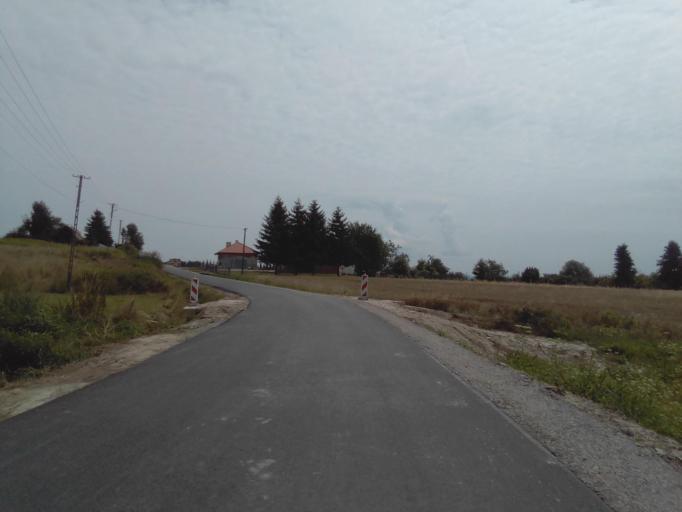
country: PL
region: Subcarpathian Voivodeship
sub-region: Powiat jasielski
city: Tarnowiec
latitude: 49.7736
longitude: 21.5858
